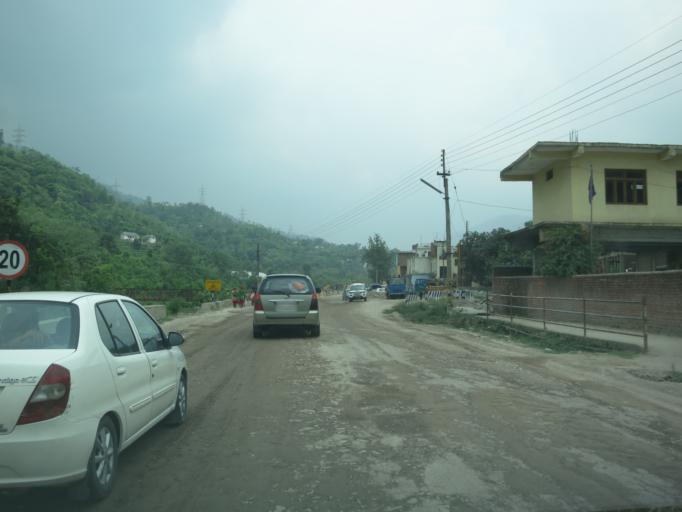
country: IN
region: Himachal Pradesh
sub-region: Mandi
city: Sundarnagar
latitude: 31.4598
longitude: 76.8609
